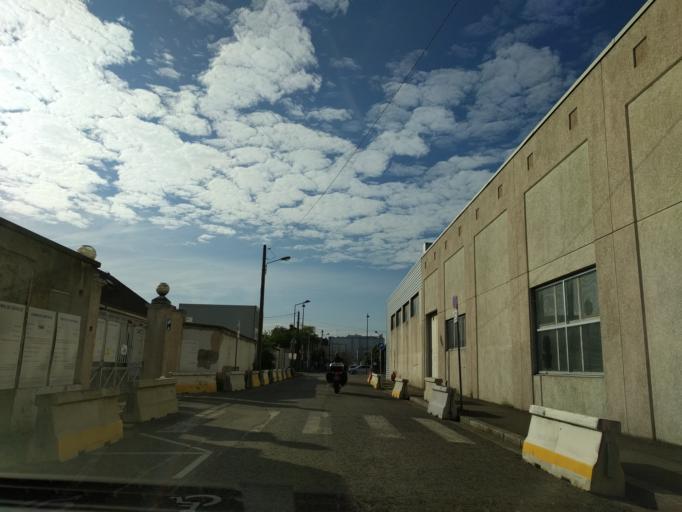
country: FR
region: Rhone-Alpes
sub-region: Departement du Rhone
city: Villeurbanne
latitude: 45.7579
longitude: 4.9018
